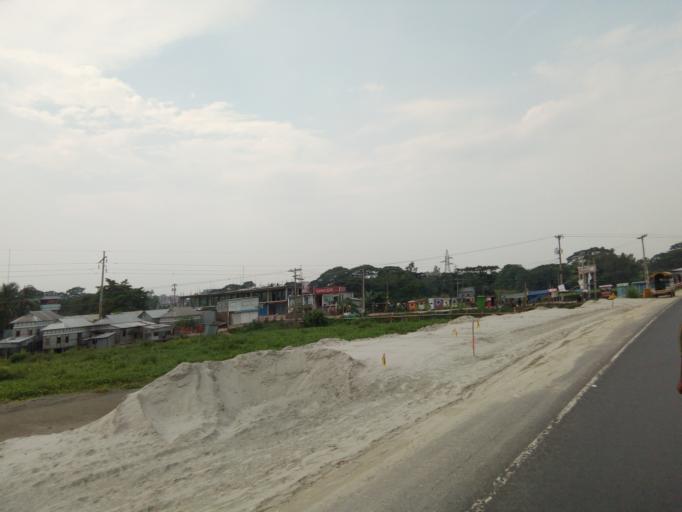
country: BD
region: Dhaka
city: Dohar
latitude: 23.5349
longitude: 90.2909
